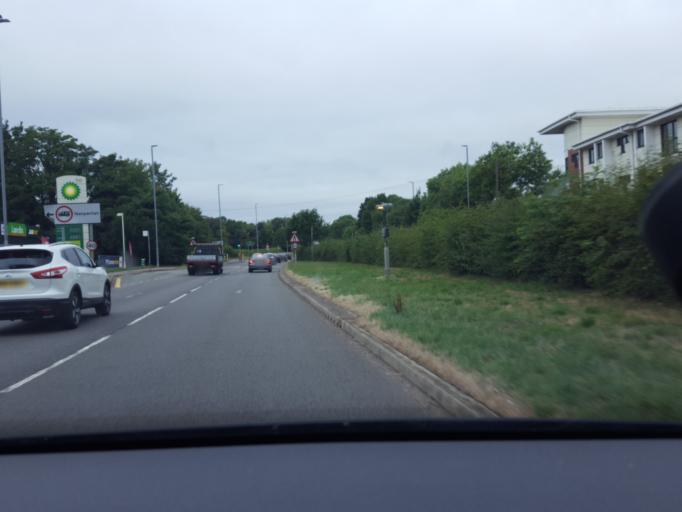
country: GB
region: England
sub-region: Leicestershire
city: Shepshed
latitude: 52.7614
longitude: -1.2575
